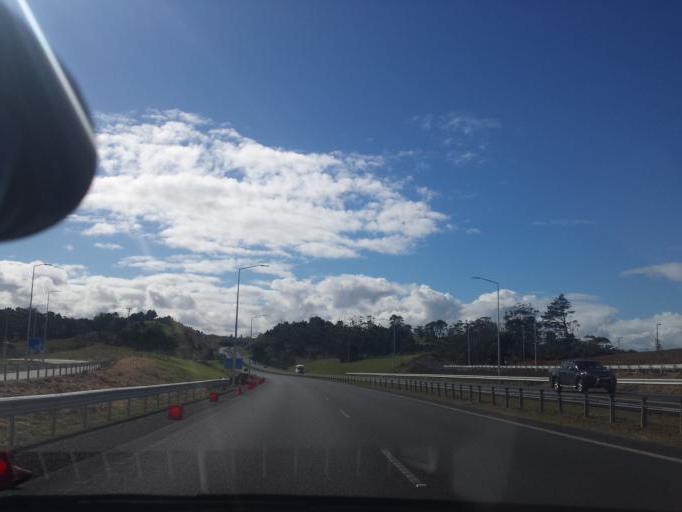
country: NZ
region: Auckland
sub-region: Auckland
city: Rothesay Bay
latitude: -36.6032
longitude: 174.6621
